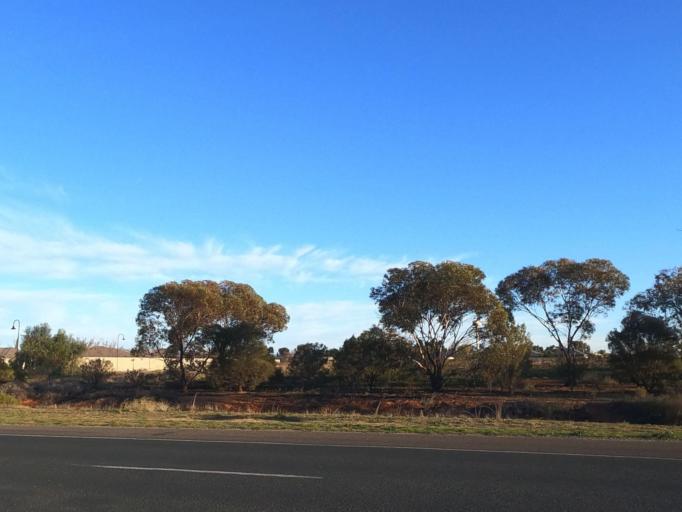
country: AU
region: Victoria
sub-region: Swan Hill
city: Swan Hill
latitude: -35.3347
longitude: 143.5318
